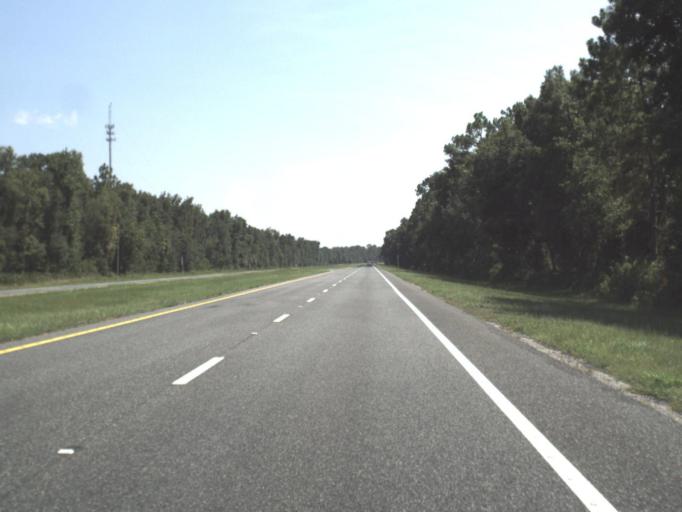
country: US
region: Florida
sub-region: Levy County
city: Inglis
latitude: 29.1025
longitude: -82.6363
